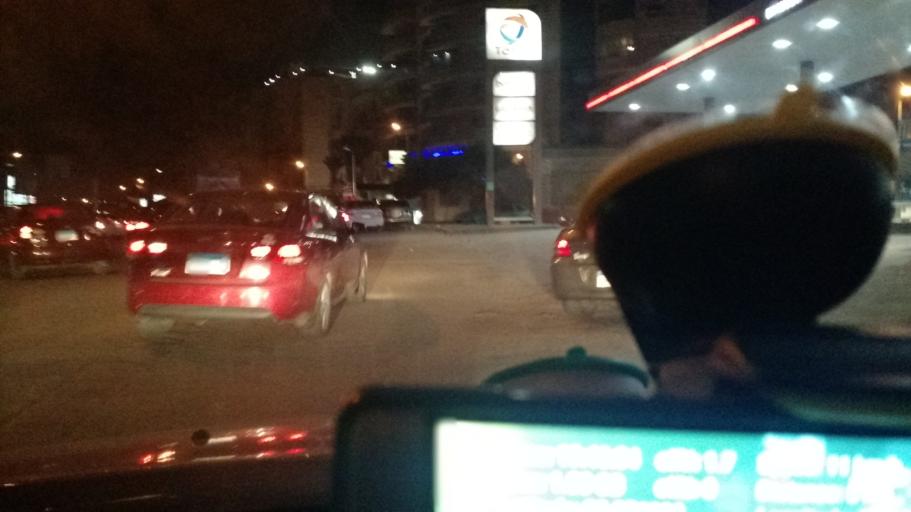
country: EG
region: Al Jizah
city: Al Jizah
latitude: 29.9761
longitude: 31.2860
